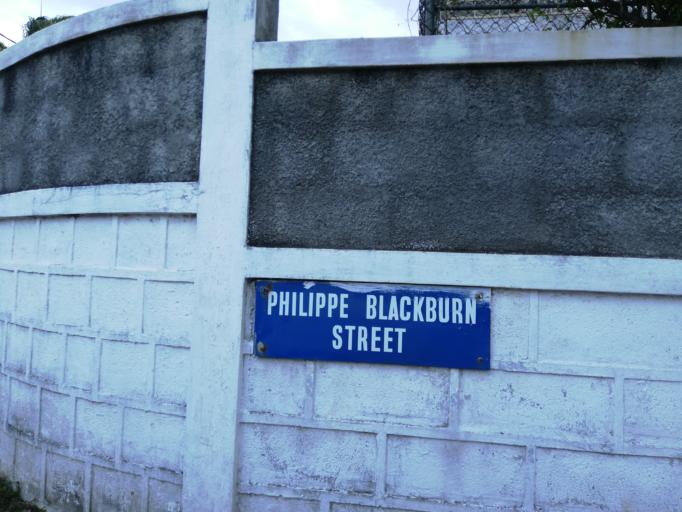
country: MU
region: Plaines Wilhems
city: Ebene
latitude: -20.2359
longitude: 57.4609
